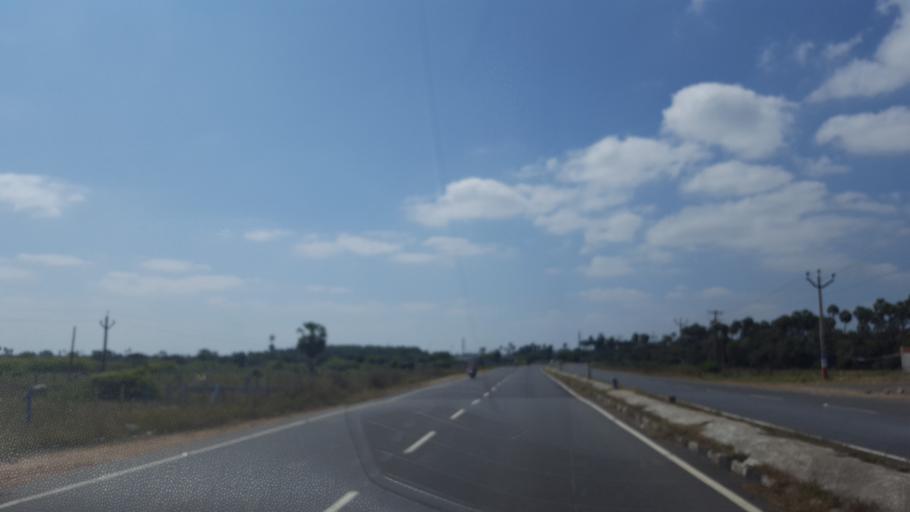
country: IN
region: Tamil Nadu
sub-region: Kancheepuram
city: Mamallapuram
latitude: 12.6237
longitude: 80.1706
